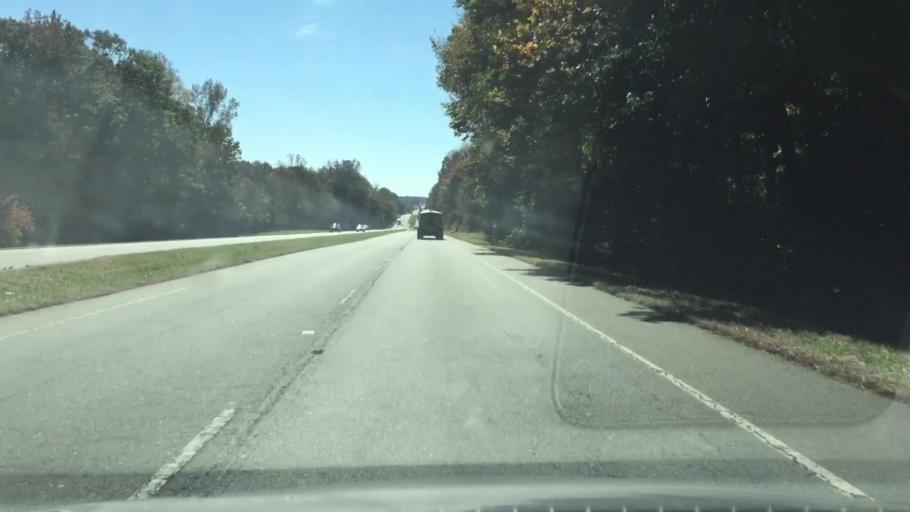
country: US
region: North Carolina
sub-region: Guilford County
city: McLeansville
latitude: 36.1966
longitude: -79.6990
